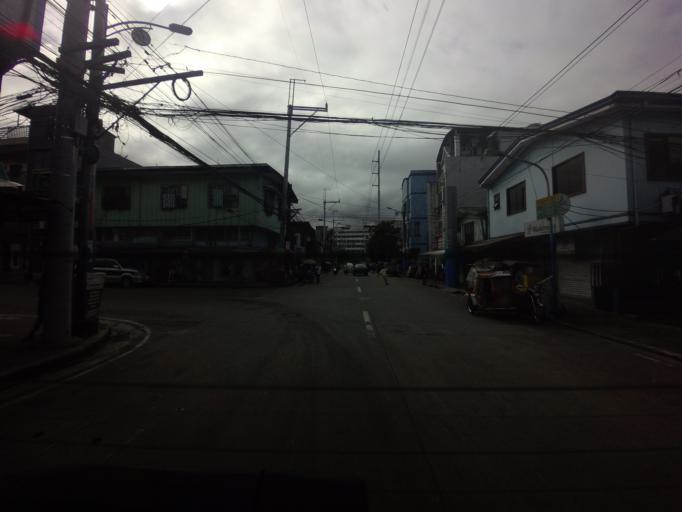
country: PH
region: Metro Manila
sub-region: City of Manila
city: Quiapo
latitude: 14.6031
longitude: 121.0011
